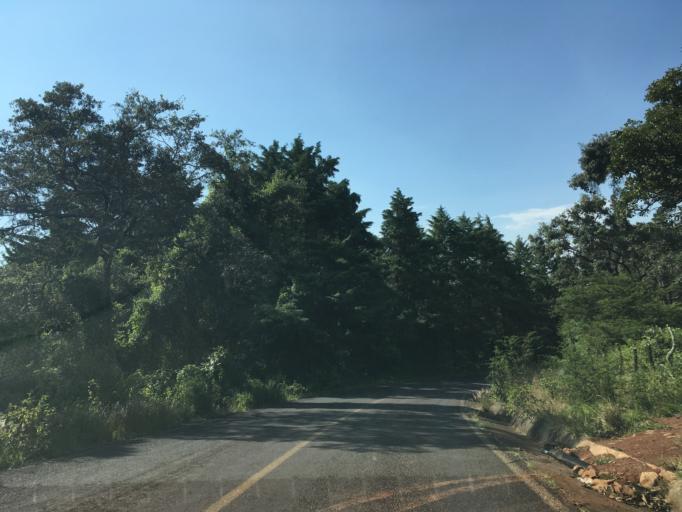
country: MX
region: Michoacan
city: Acuitzio del Canje
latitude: 19.5463
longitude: -101.2597
